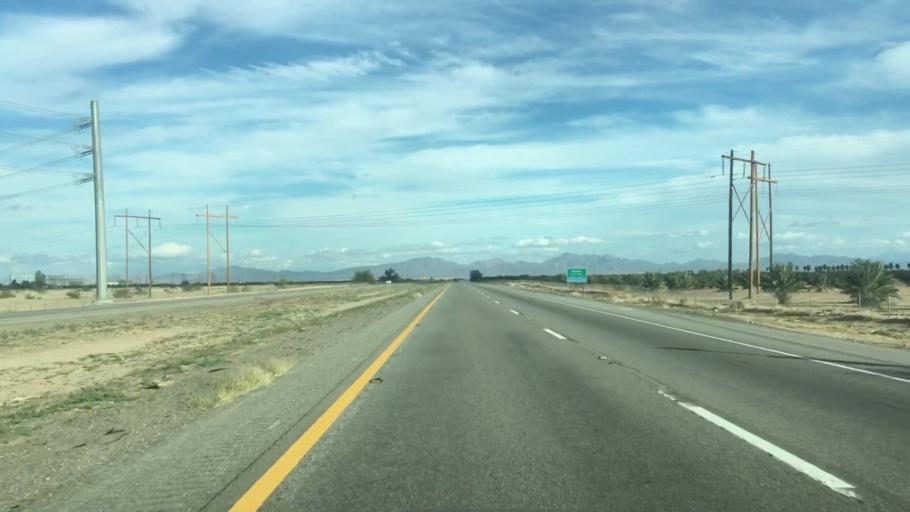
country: US
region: California
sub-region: Riverside County
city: Mesa Verde
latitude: 33.6066
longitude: -114.6933
